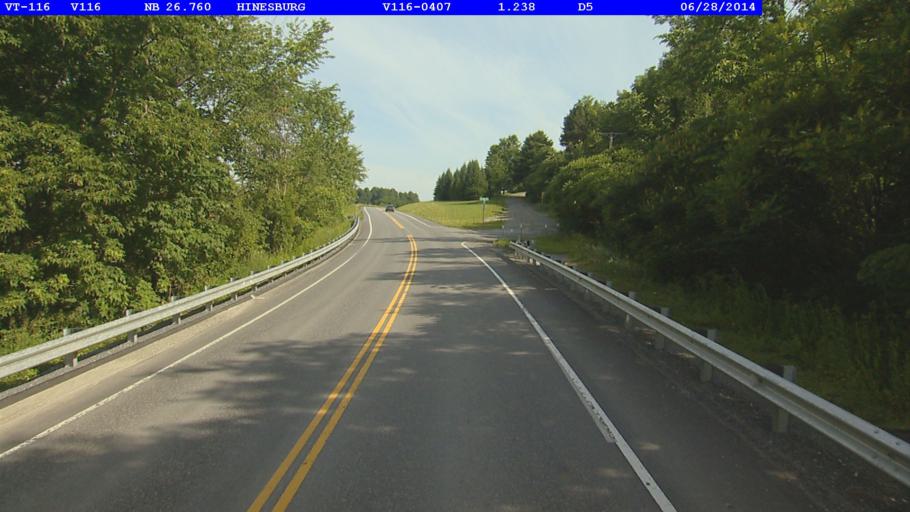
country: US
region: Vermont
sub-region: Chittenden County
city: Hinesburg
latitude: 44.2976
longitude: -73.0727
